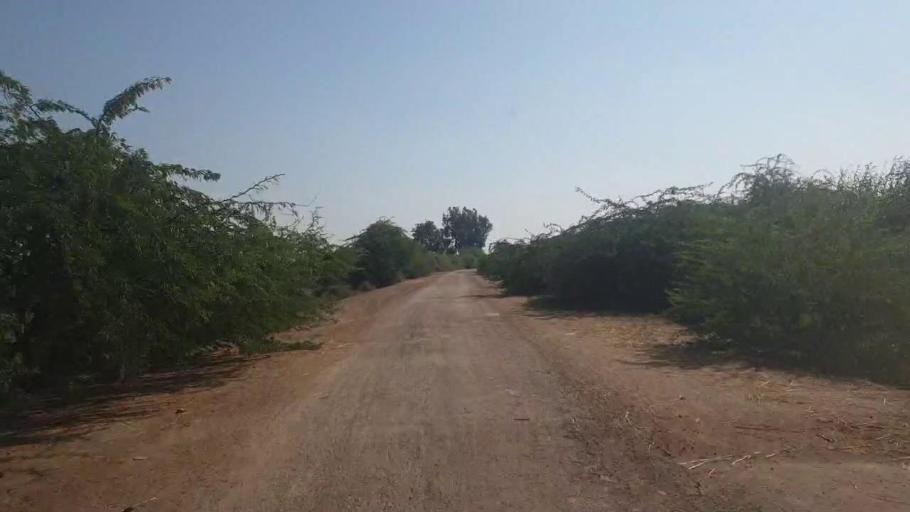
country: PK
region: Sindh
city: Badin
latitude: 24.5716
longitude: 68.8450
